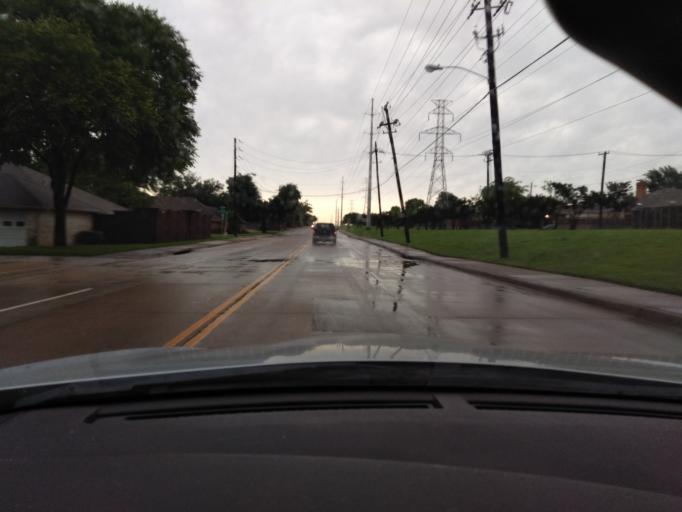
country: US
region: Texas
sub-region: Dallas County
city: Addison
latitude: 32.9819
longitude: -96.7787
